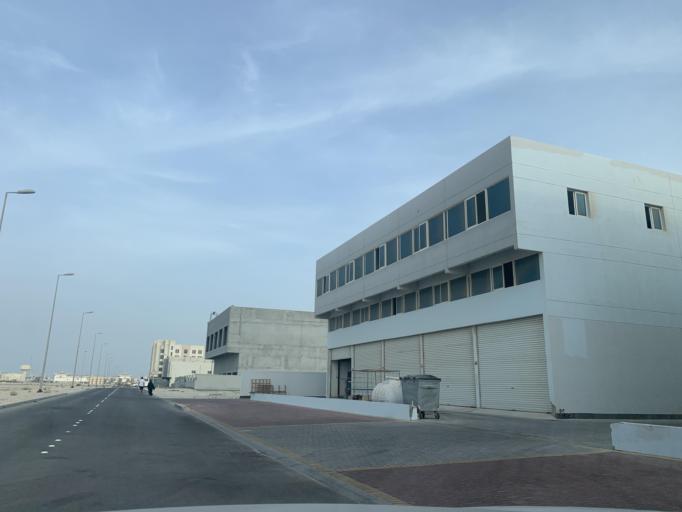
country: BH
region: Muharraq
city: Al Muharraq
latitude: 26.3102
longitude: 50.6190
